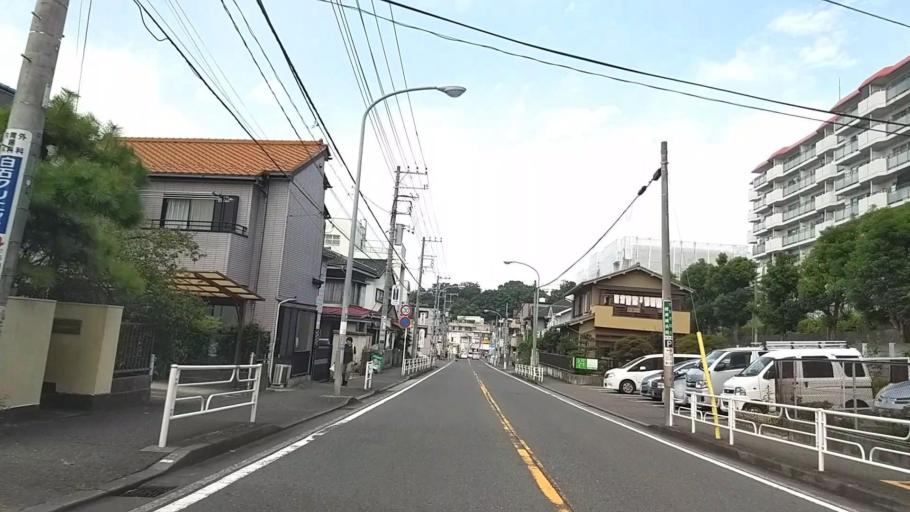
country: JP
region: Kanagawa
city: Yokohama
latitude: 35.4151
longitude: 139.5760
